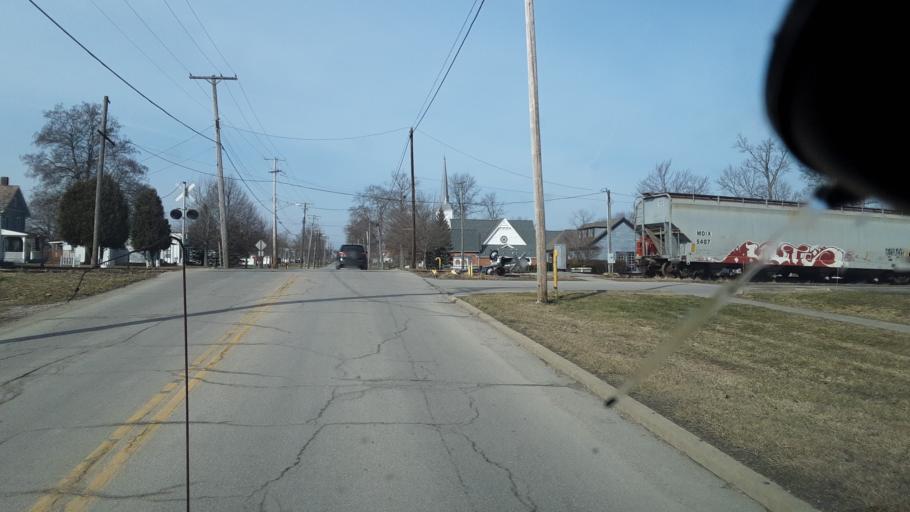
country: US
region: Ohio
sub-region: Ashtabula County
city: Jefferson
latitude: 41.7384
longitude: -80.7609
